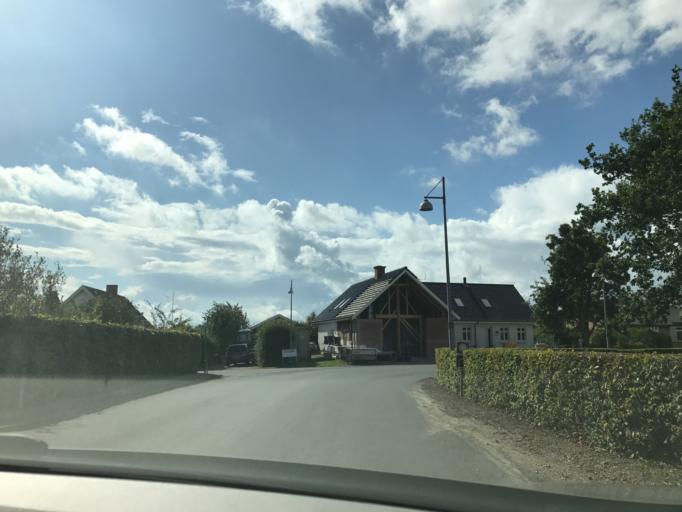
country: DK
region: South Denmark
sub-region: Middelfart Kommune
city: Norre Aby
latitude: 55.4628
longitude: 9.8014
